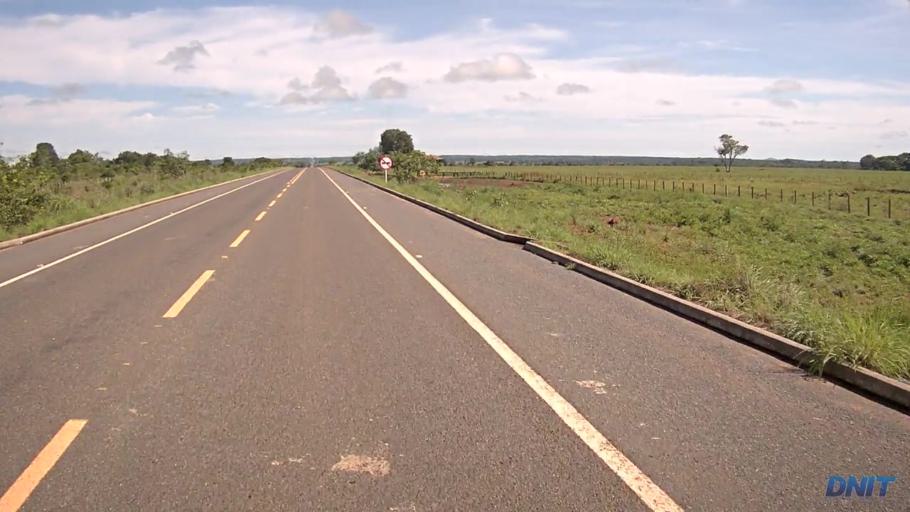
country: BR
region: Goias
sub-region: Sao Miguel Do Araguaia
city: Sao Miguel do Araguaia
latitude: -13.4129
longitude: -50.1315
